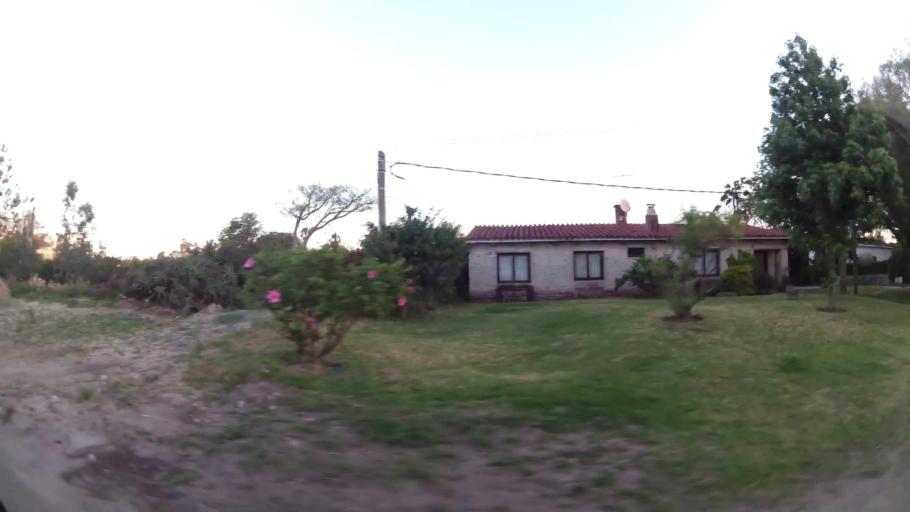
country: UY
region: Canelones
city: Barra de Carrasco
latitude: -34.8315
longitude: -55.9619
